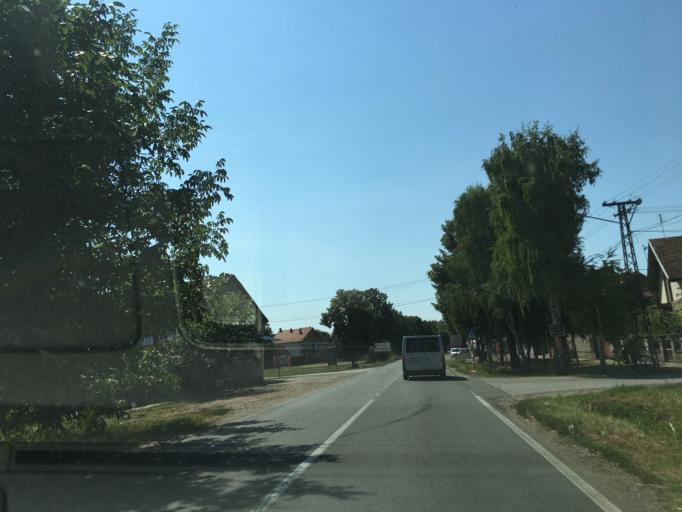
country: RS
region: Central Serbia
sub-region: Belgrade
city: Grocka
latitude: 44.7614
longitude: 20.7347
